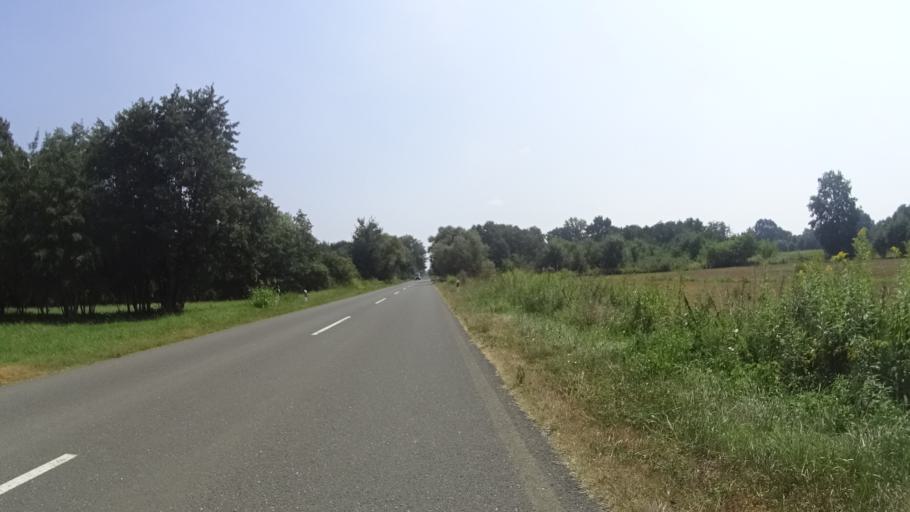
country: HR
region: Medimurska
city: Gorican
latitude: 46.4055
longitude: 16.6694
